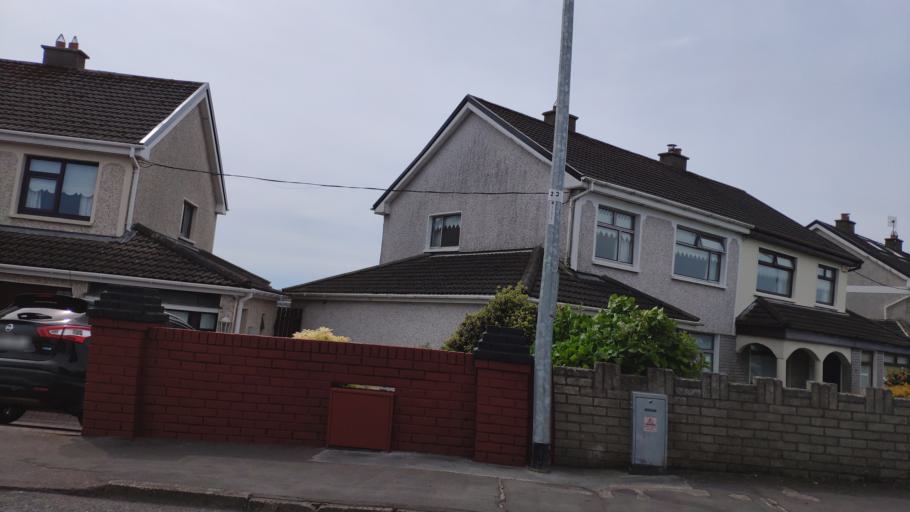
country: IE
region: Munster
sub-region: County Cork
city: Cork
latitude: 51.9192
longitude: -8.4632
